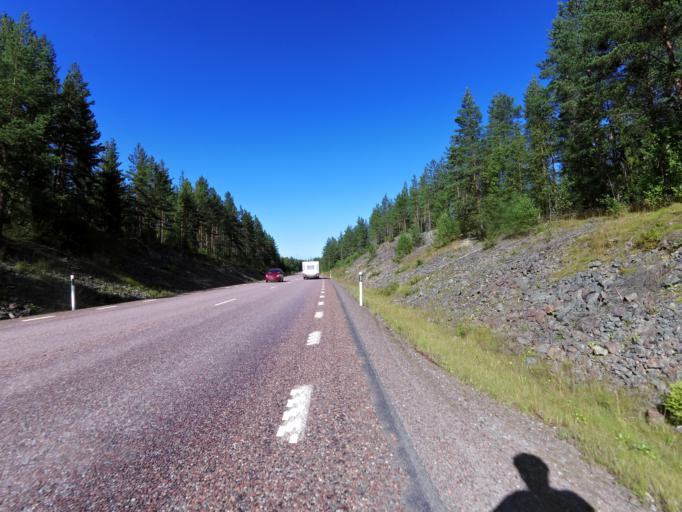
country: SE
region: Gaevleborg
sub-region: Hofors Kommun
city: Hofors
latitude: 60.5500
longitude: 16.4750
